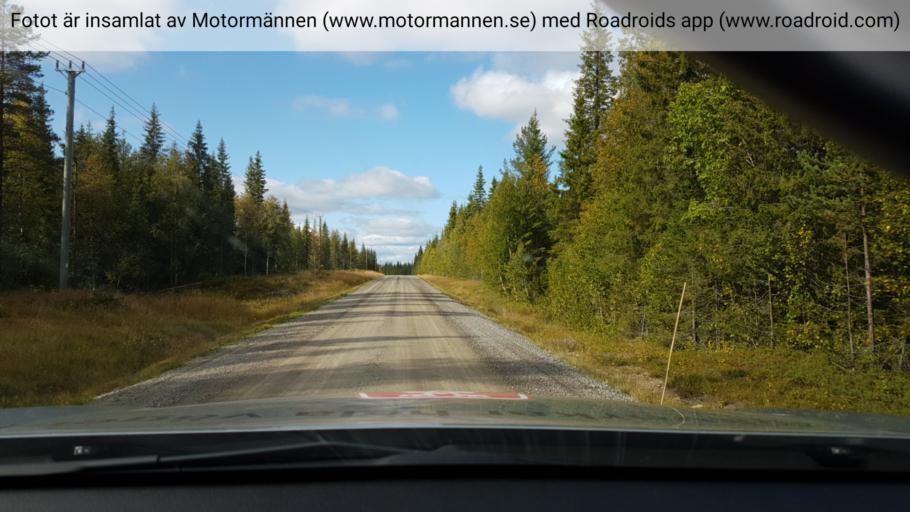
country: SE
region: Vaesterbotten
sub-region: Sorsele Kommun
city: Sorsele
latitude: 65.5148
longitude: 18.0091
